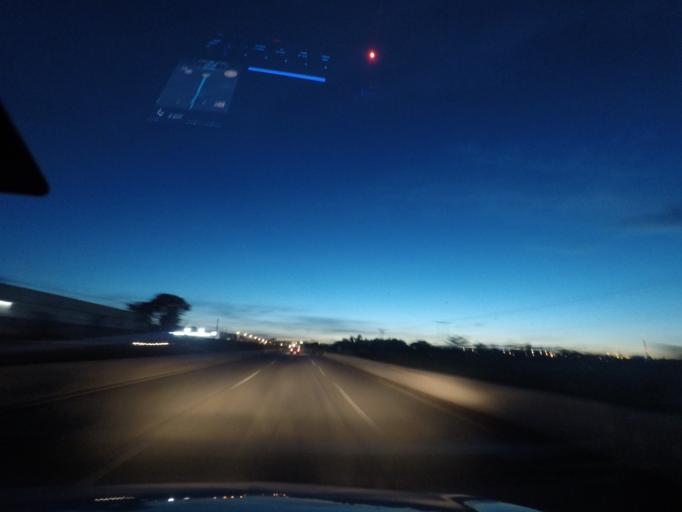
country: BR
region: Goias
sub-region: Goiania
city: Goiania
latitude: -16.7049
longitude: -49.3442
